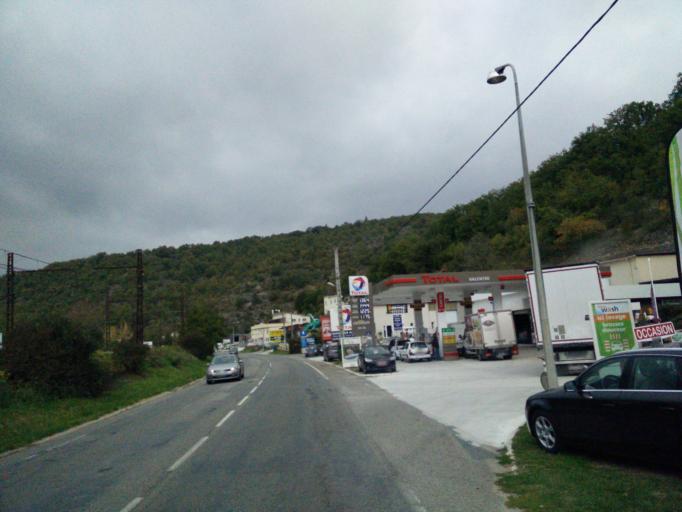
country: FR
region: Midi-Pyrenees
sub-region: Departement du Lot
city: Cahors
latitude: 44.4738
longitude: 1.4286
